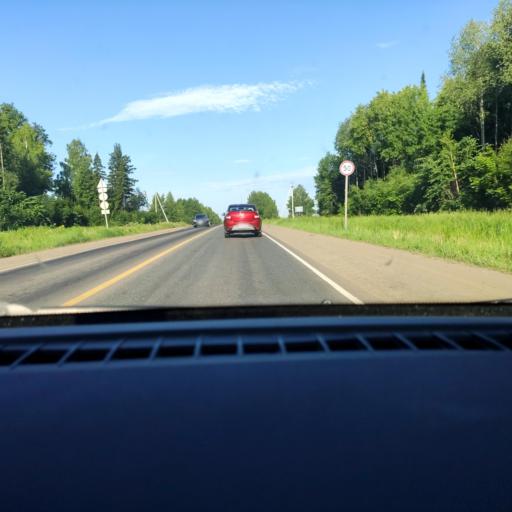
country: RU
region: Udmurtiya
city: Khokhryaki
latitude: 56.9154
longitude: 53.4222
